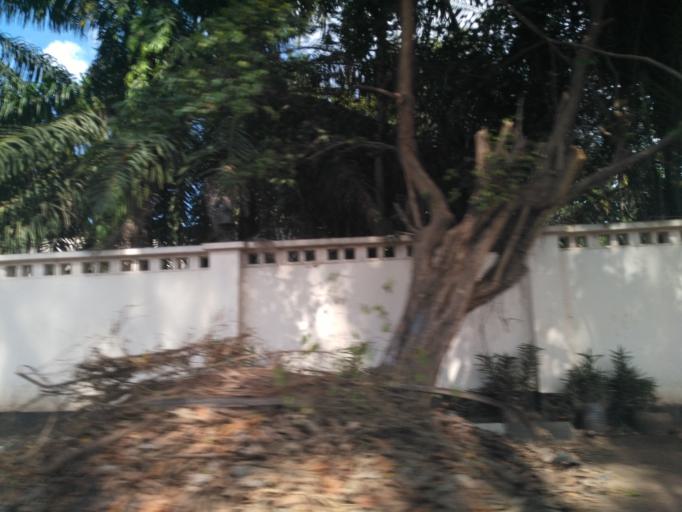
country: TZ
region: Dar es Salaam
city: Magomeni
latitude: -6.7749
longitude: 39.2598
